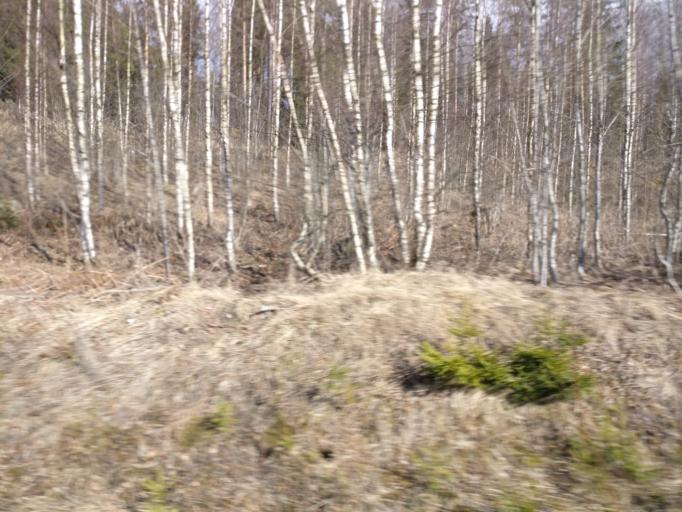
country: FI
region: Uusimaa
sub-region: Helsinki
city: Sammatti
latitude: 60.2894
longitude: 23.7655
